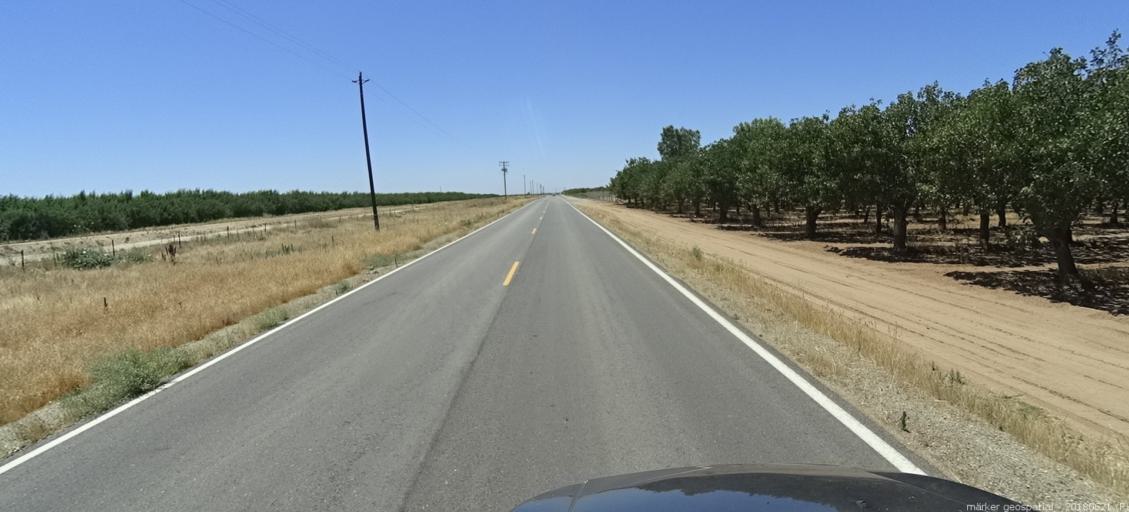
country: US
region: California
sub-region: Madera County
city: Bonadelle Ranchos-Madera Ranchos
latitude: 36.9142
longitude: -119.8942
